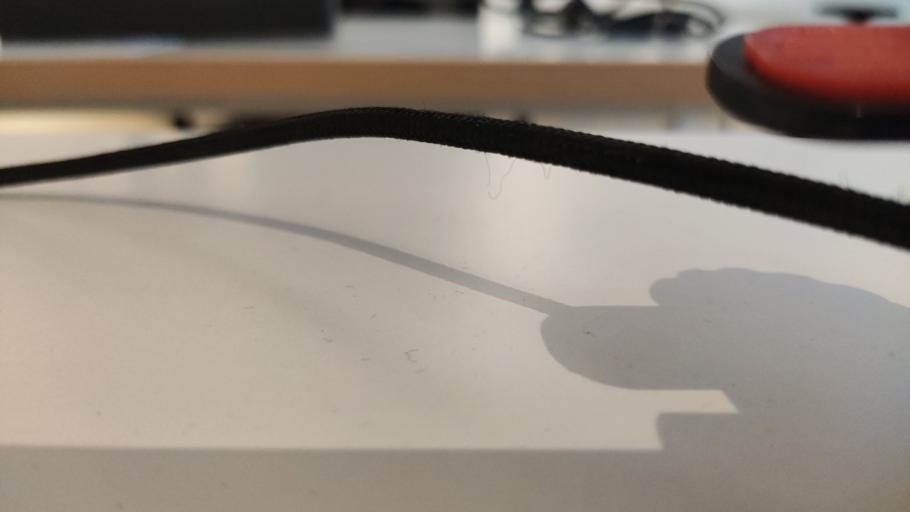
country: RU
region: Moskovskaya
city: Ruza
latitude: 55.7929
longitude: 36.2849
